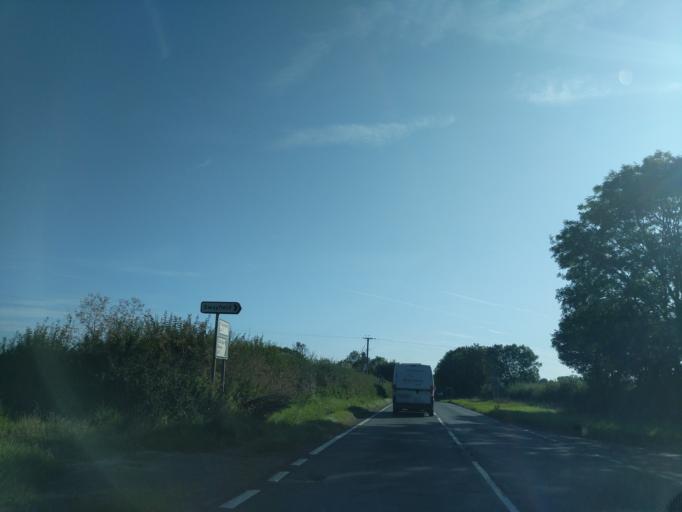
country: GB
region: England
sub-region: District of Rutland
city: Clipsham
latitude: 52.8105
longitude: -0.5318
